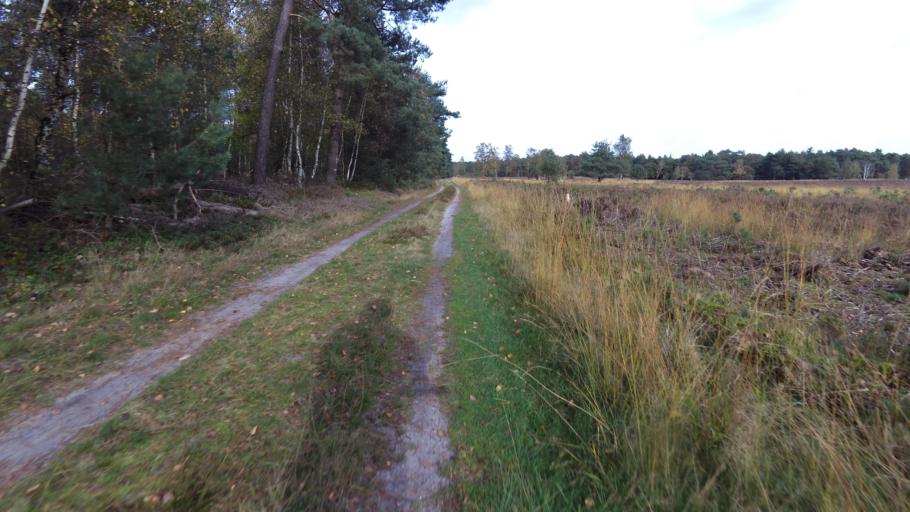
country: NL
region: Gelderland
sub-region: Gemeente Epe
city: Emst
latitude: 52.3285
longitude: 5.8804
